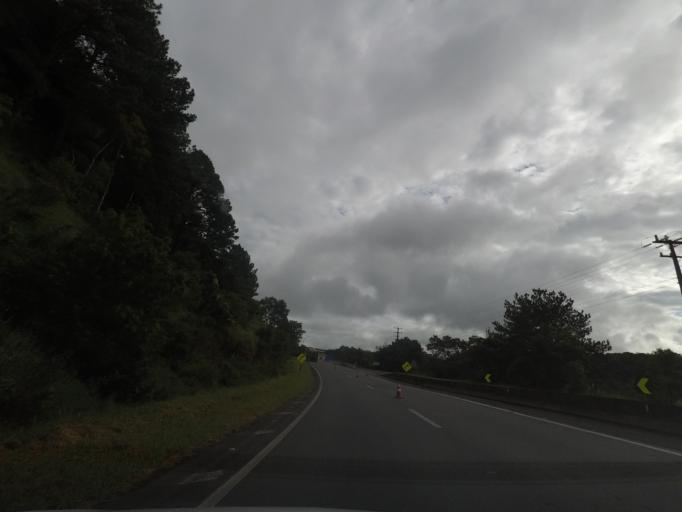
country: BR
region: Parana
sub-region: Campina Grande Do Sul
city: Campina Grande do Sul
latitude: -25.1826
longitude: -48.8790
